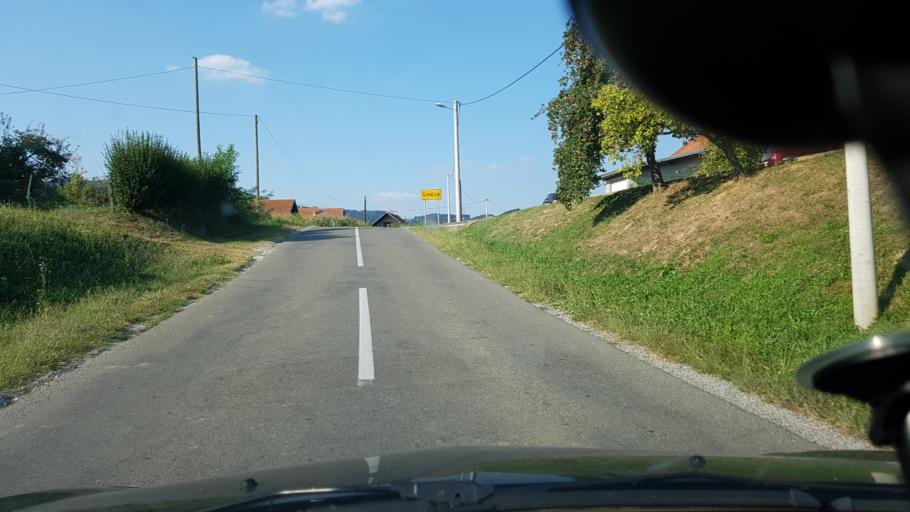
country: SI
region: Bistrica ob Sotli
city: Bistrica ob Sotli
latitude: 46.0296
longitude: 15.7324
